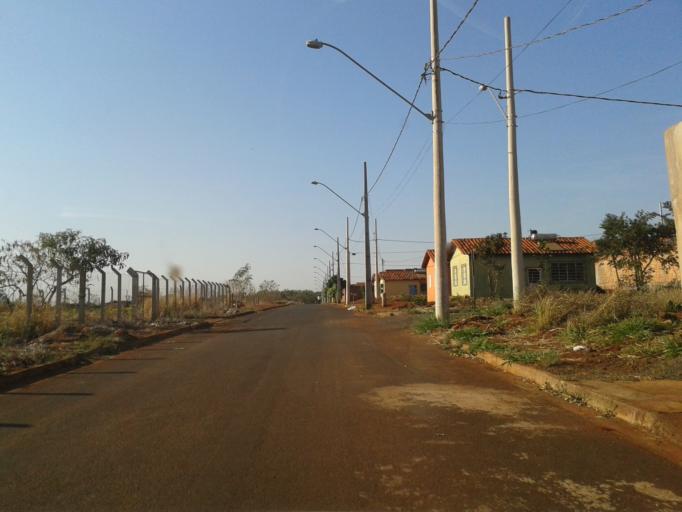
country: BR
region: Minas Gerais
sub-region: Ituiutaba
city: Ituiutaba
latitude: -18.9844
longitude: -49.4252
